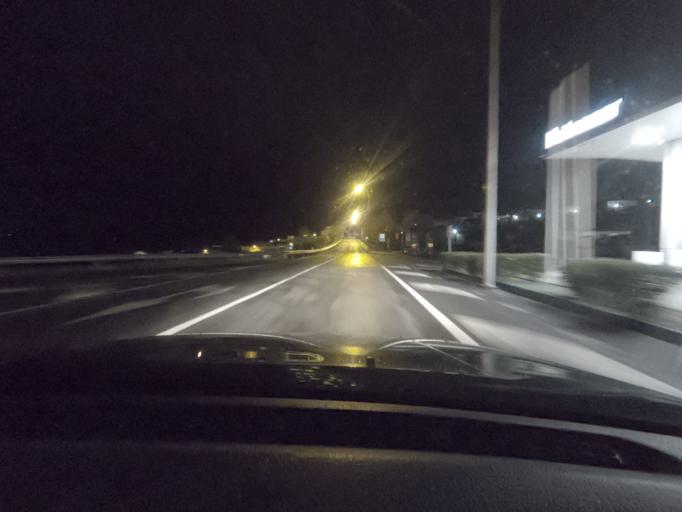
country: ES
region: Extremadura
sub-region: Provincia de Caceres
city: Canaveral
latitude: 39.7946
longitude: -6.3853
